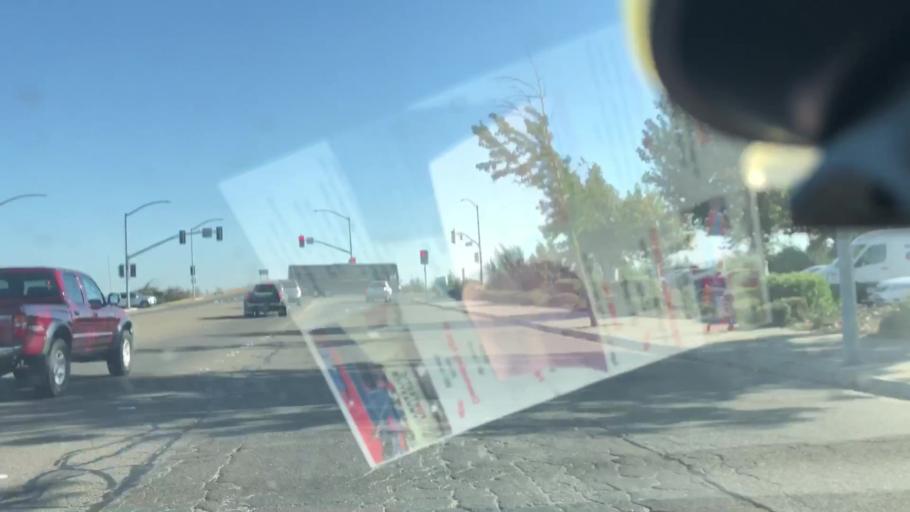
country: US
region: California
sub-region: San Joaquin County
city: Manteca
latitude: 37.7861
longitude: -121.2161
